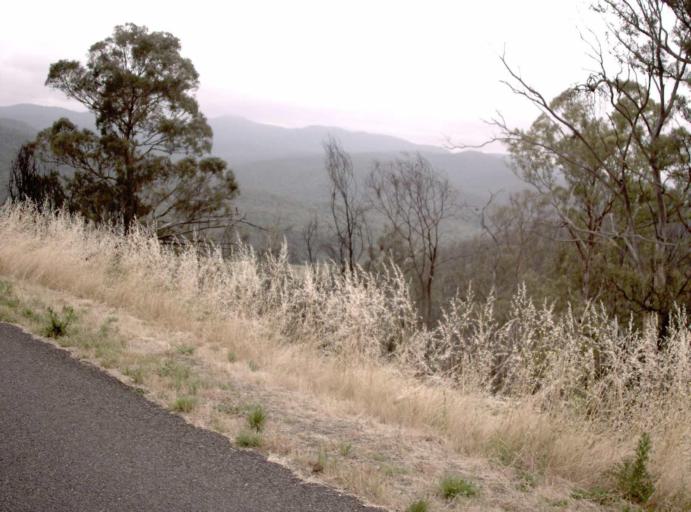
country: AU
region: Victoria
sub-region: Wellington
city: Heyfield
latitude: -37.8227
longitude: 146.6755
